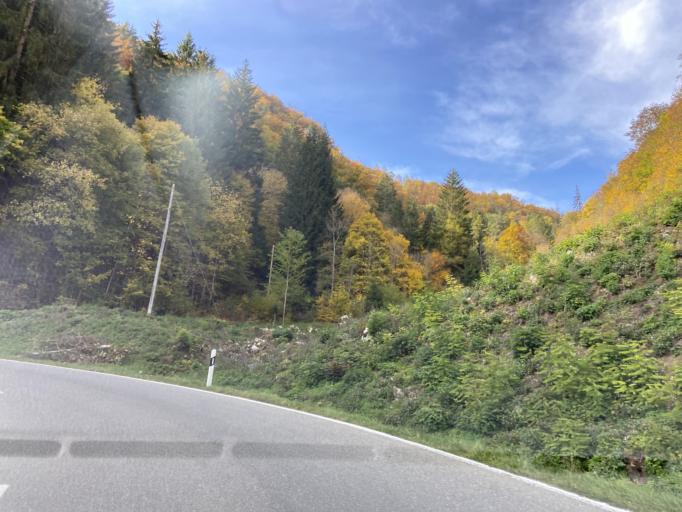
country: DE
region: Baden-Wuerttemberg
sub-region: Tuebingen Region
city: Schwenningen
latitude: 48.0885
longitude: 9.0356
